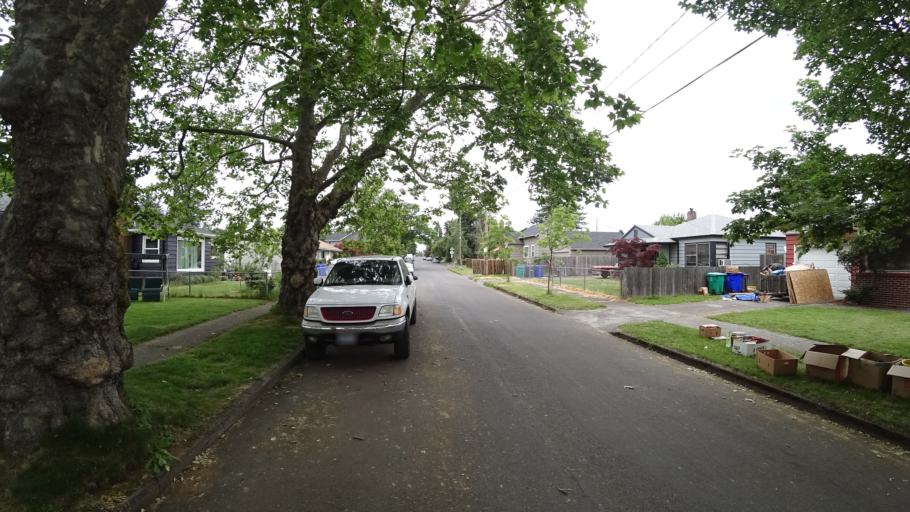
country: US
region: Oregon
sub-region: Multnomah County
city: Lents
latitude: 45.4852
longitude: -122.5769
